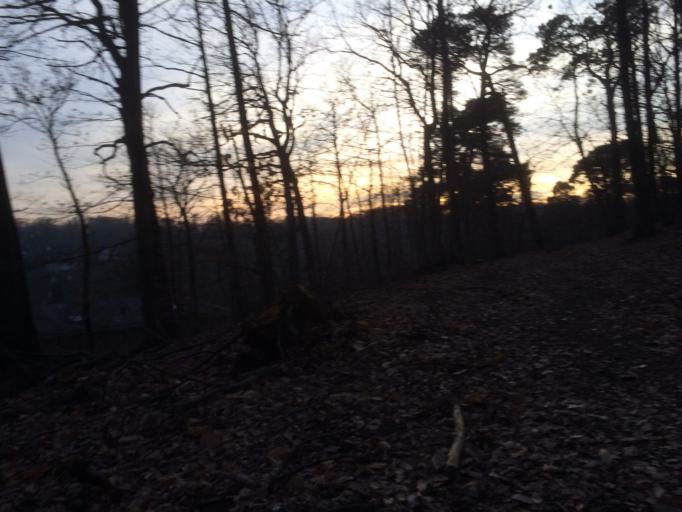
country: FR
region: Ile-de-France
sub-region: Departement de l'Essonne
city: Verrieres-le-Buisson
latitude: 48.7511
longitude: 2.2539
